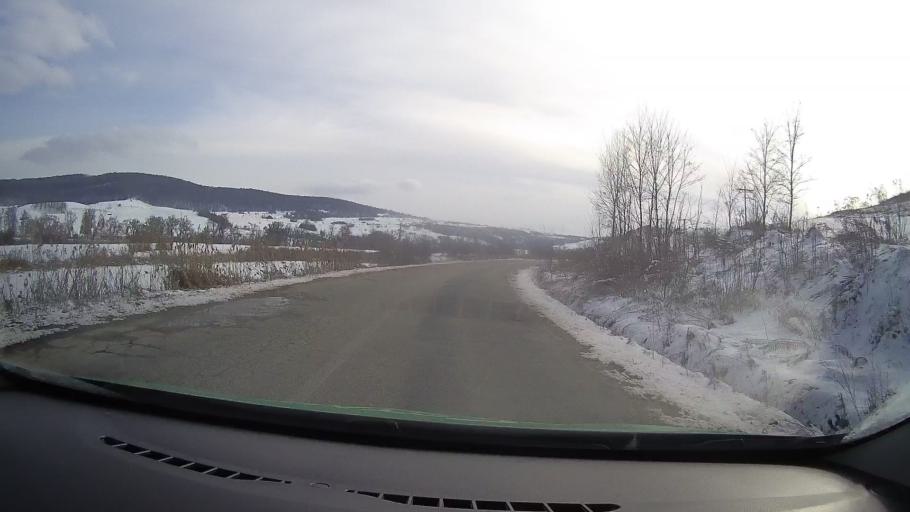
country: RO
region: Sibiu
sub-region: Comuna Iacobeni
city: Iacobeni
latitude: 46.0238
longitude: 24.7069
